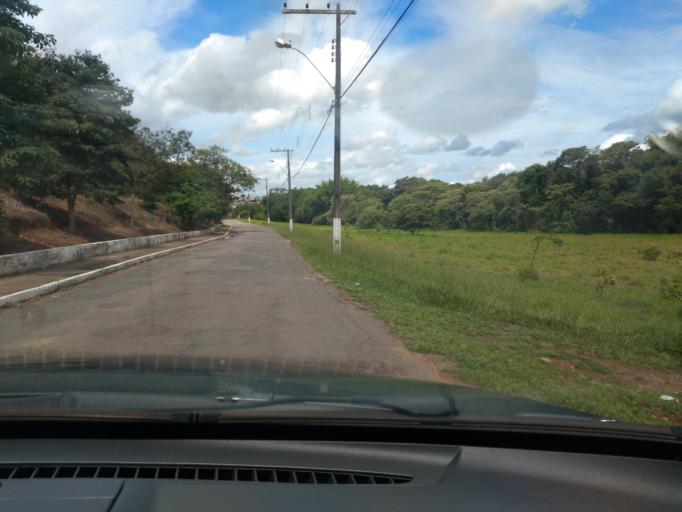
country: BR
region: Minas Gerais
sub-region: Tres Coracoes
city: Tres Coracoes
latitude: -21.7004
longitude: -45.2699
